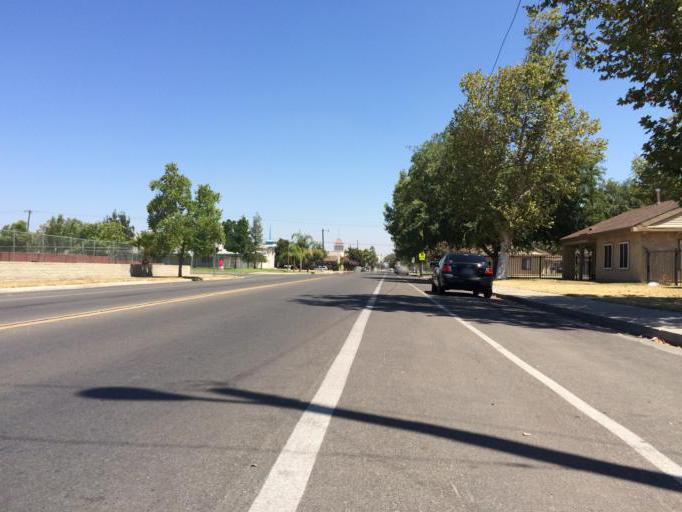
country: US
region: California
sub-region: Fresno County
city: Fresno
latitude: 36.7250
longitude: -119.8026
